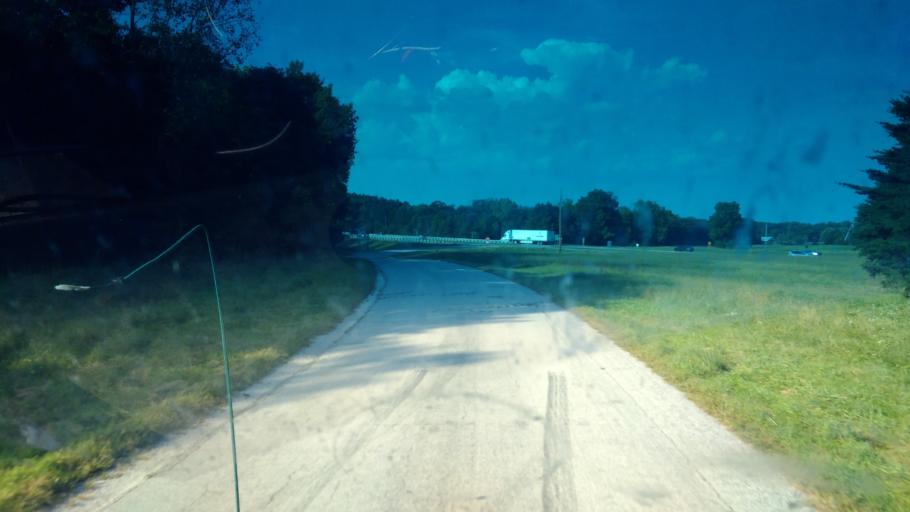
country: US
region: Ohio
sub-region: Wyandot County
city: Carey
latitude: 40.9148
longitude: -83.3544
